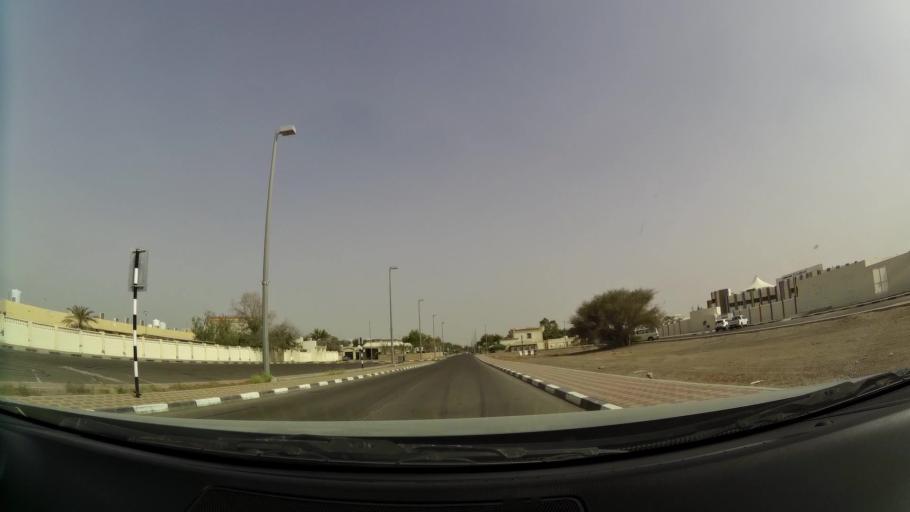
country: AE
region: Abu Dhabi
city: Al Ain
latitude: 24.1843
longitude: 55.6159
